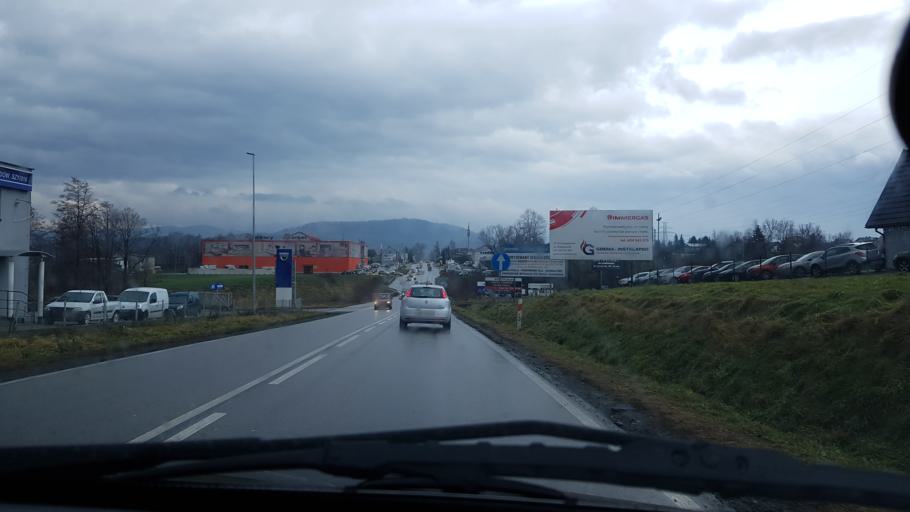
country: PL
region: Silesian Voivodeship
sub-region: Powiat zywiecki
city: Zywiec
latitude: 49.6959
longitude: 19.1803
